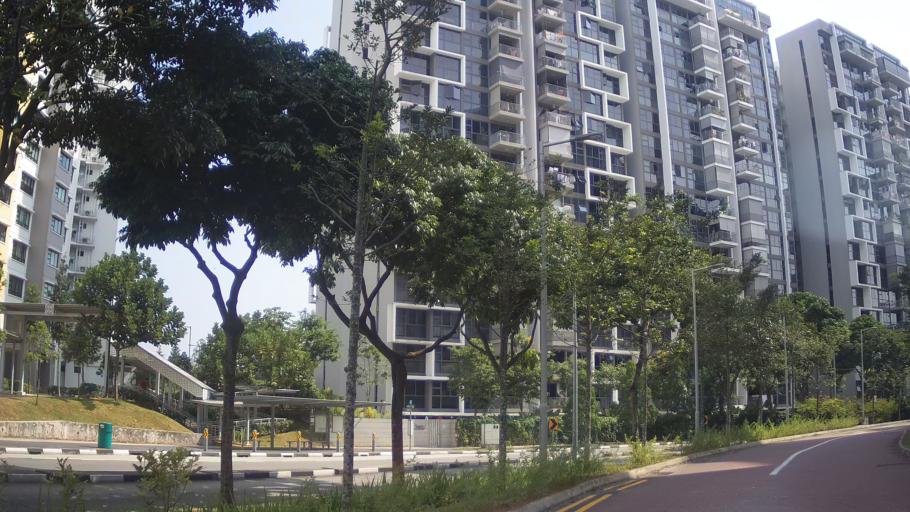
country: MY
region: Johor
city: Johor Bahru
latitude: 1.3888
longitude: 103.7689
